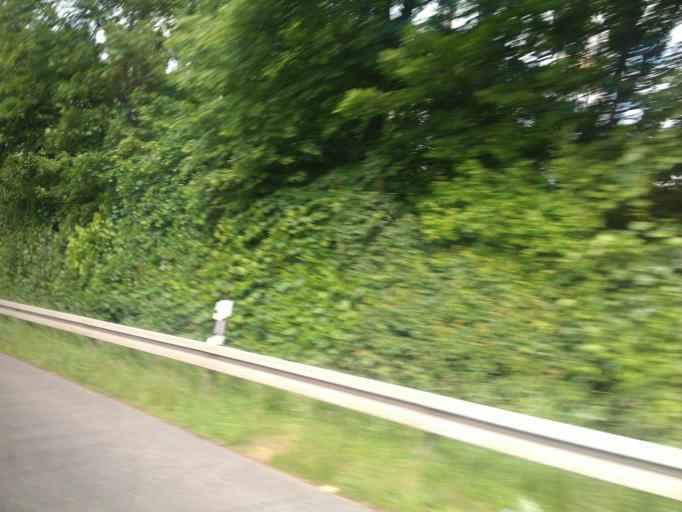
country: DE
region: North Rhine-Westphalia
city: Wesseling
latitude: 50.8401
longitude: 6.9670
